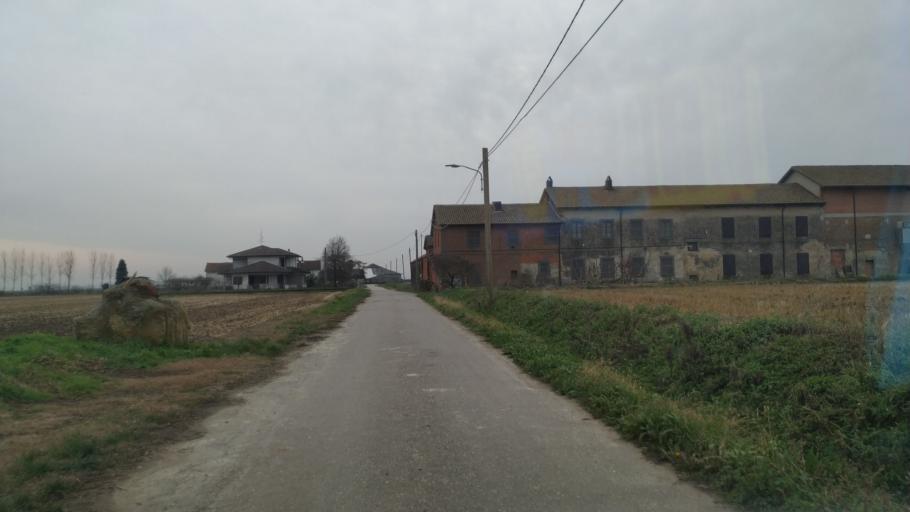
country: IT
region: Piedmont
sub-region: Provincia di Vercelli
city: Sali Vercellese
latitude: 45.3078
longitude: 8.3266
